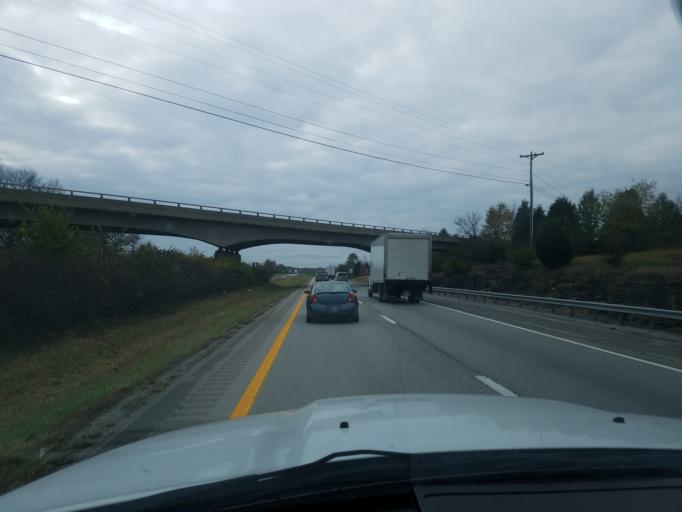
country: US
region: Kentucky
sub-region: Oldham County
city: La Grange
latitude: 38.4495
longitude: -85.3041
